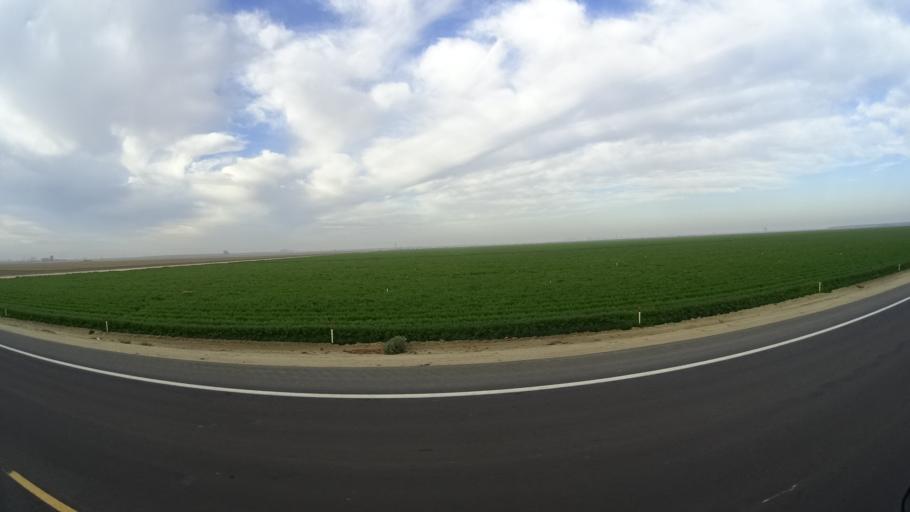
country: US
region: California
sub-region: Kern County
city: Rosedale
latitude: 35.4056
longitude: -119.1987
